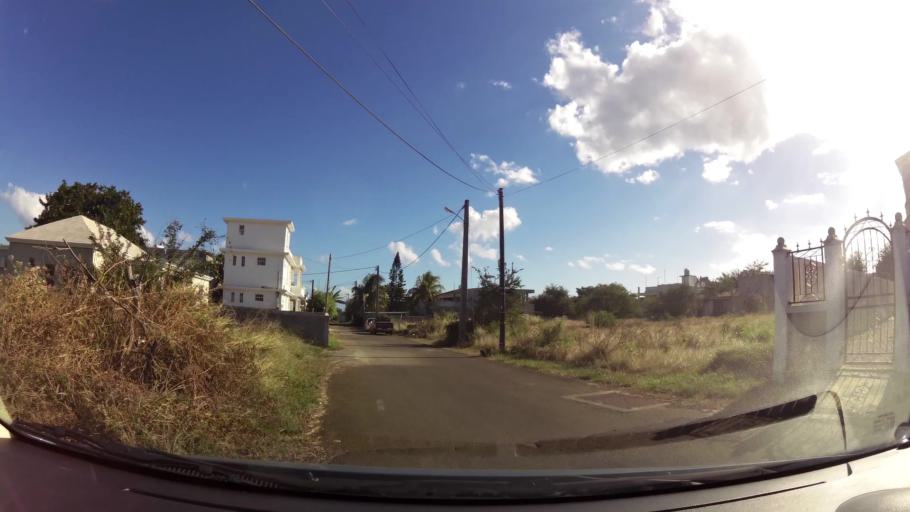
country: MU
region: Black River
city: Albion
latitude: -20.2042
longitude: 57.4115
